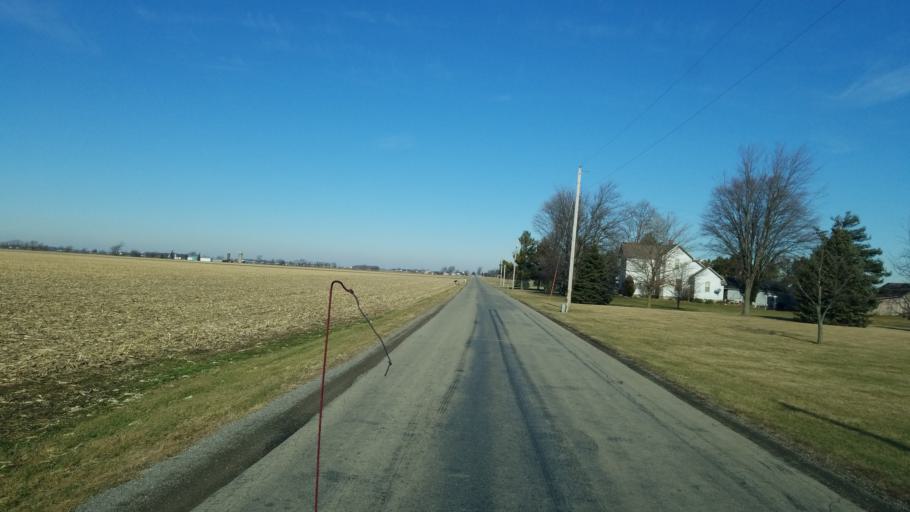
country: US
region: Ohio
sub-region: Putnam County
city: Leipsic
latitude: 41.1238
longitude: -83.9769
